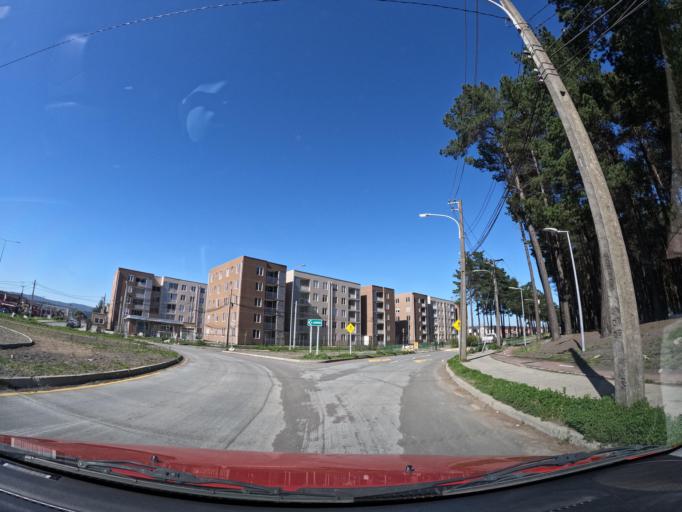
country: CL
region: Biobio
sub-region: Provincia de Concepcion
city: Concepcion
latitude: -36.8821
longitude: -73.1496
